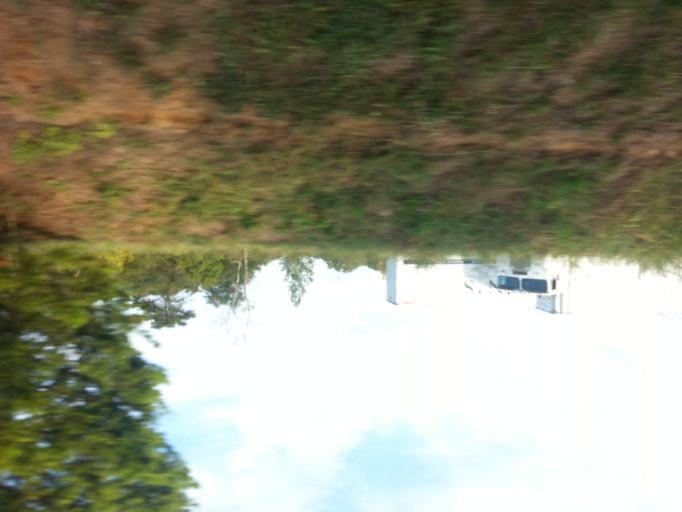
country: US
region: Tennessee
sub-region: Blount County
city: Wildwood
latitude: 35.8413
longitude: -83.8690
